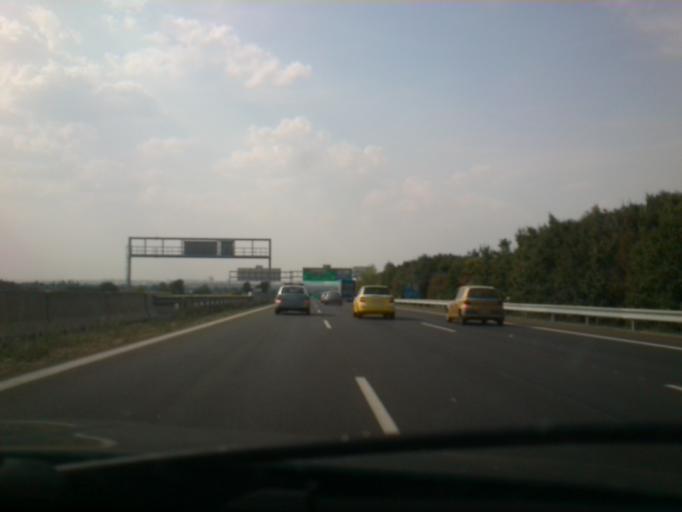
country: CZ
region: Central Bohemia
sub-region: Okres Praha-Zapad
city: Pruhonice
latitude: 49.9968
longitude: 14.5815
